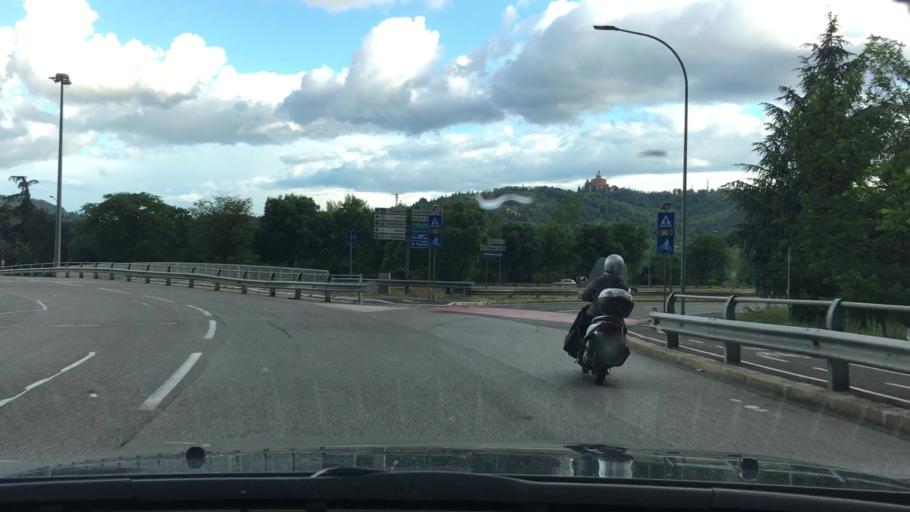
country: IT
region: Emilia-Romagna
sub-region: Provincia di Bologna
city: Bologna
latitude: 44.5005
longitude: 11.3035
